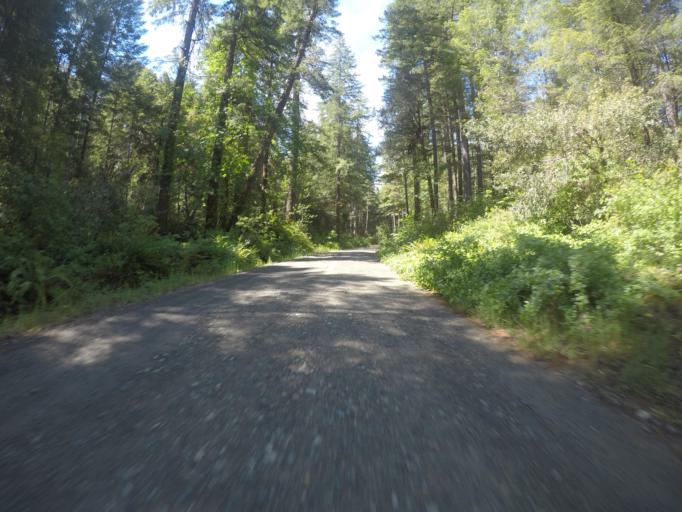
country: US
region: California
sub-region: Del Norte County
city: Bertsch-Oceanview
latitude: 41.6934
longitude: -123.9032
